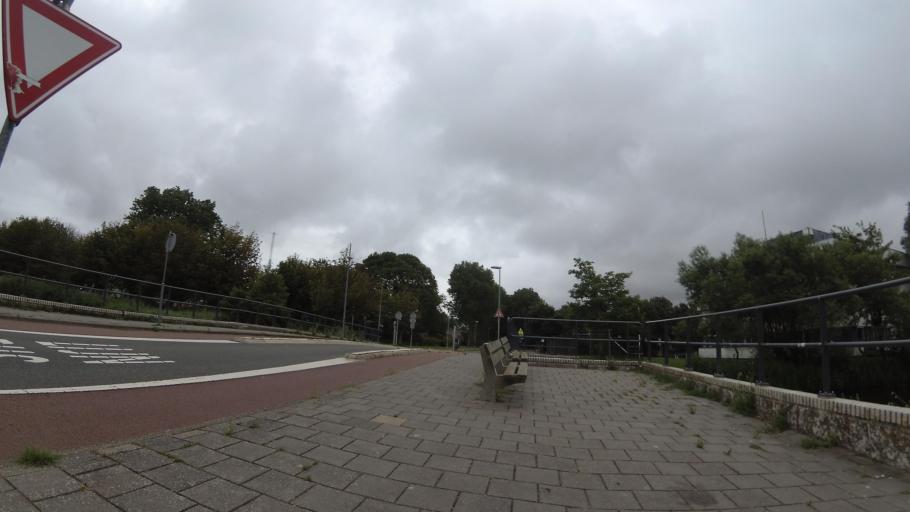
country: NL
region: North Holland
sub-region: Gemeente Den Helder
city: Den Helder
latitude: 52.9406
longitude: 4.7490
